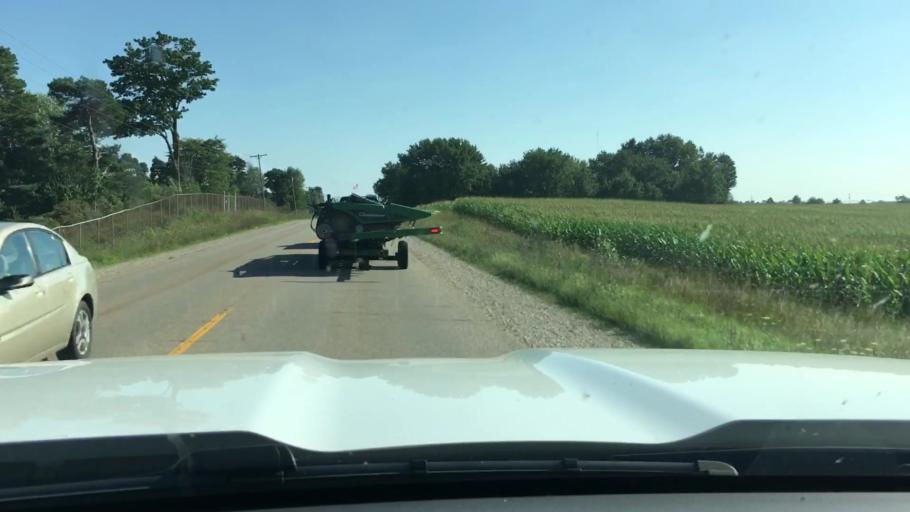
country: US
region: Michigan
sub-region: Ottawa County
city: Coopersville
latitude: 43.0658
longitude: -85.9569
